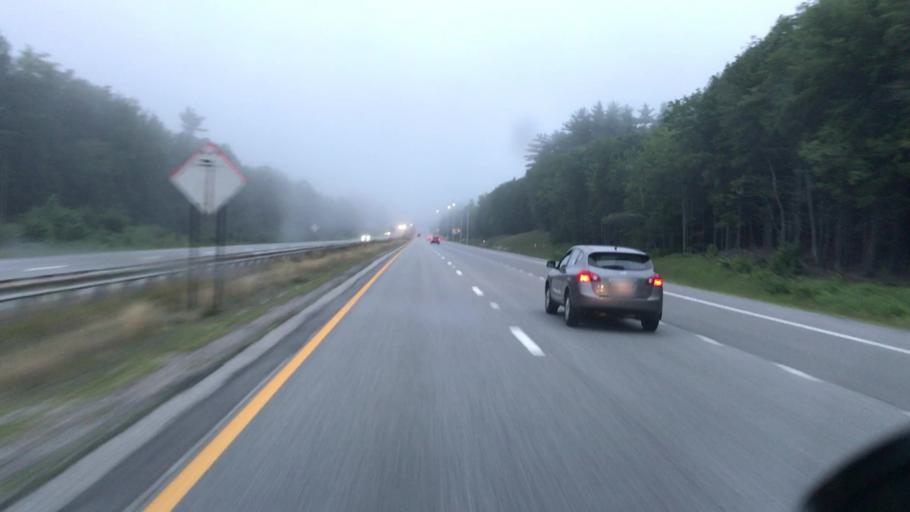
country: US
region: Maine
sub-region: Cumberland County
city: Cumberland Center
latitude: 43.8273
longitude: -70.3217
